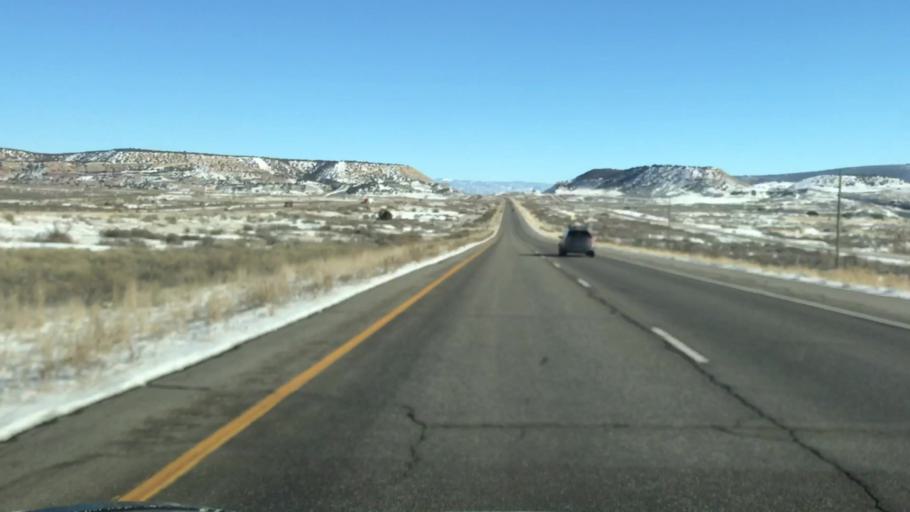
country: US
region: Colorado
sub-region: Garfield County
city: Rifle
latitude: 39.5018
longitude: -107.9047
